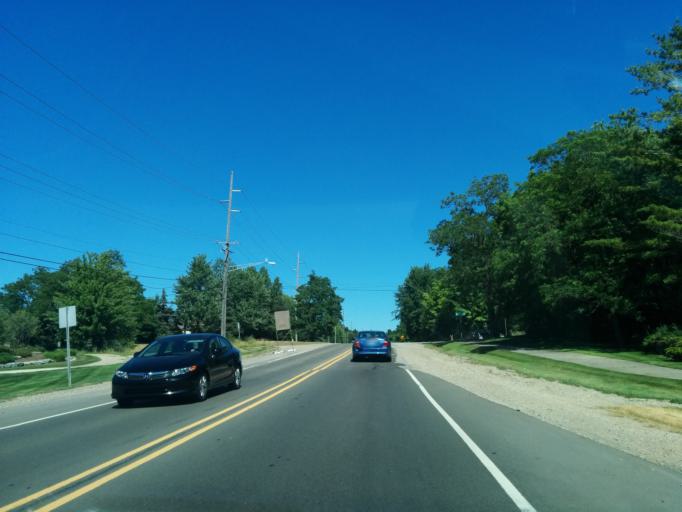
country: US
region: Michigan
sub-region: Oakland County
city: West Bloomfield Township
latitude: 42.5413
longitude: -83.4211
